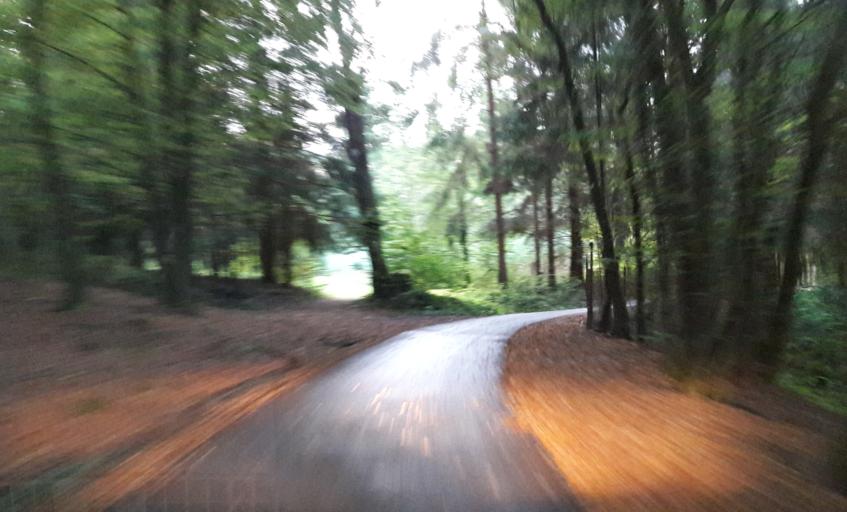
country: DE
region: Rheinland-Pfalz
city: Breitenbach
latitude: 49.4424
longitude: 7.2289
